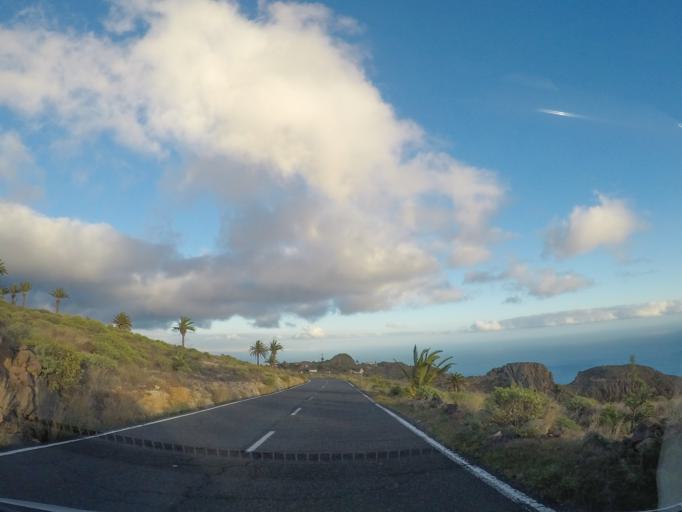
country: ES
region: Canary Islands
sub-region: Provincia de Santa Cruz de Tenerife
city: Alajero
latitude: 28.0572
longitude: -17.2304
